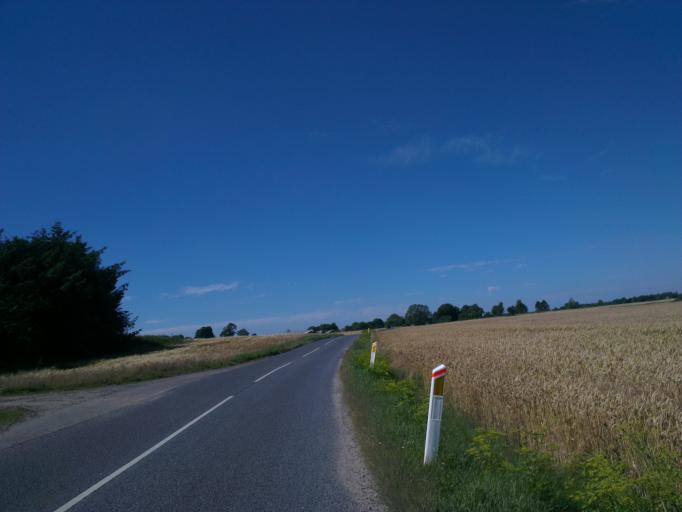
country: DK
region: Capital Region
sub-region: Frederikssund Kommune
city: Frederikssund
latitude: 55.8563
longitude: 12.1106
